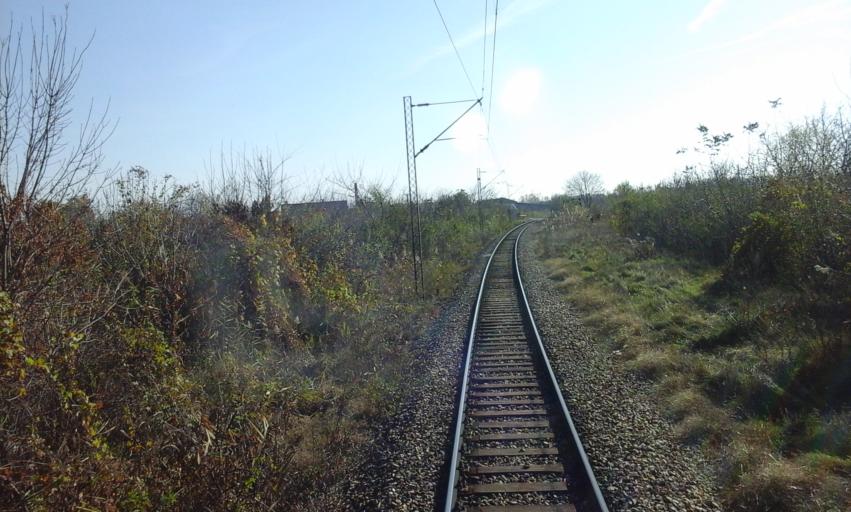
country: RS
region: Autonomna Pokrajina Vojvodina
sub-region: Severnobacki Okrug
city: Subotica
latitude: 46.0866
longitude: 19.6884
